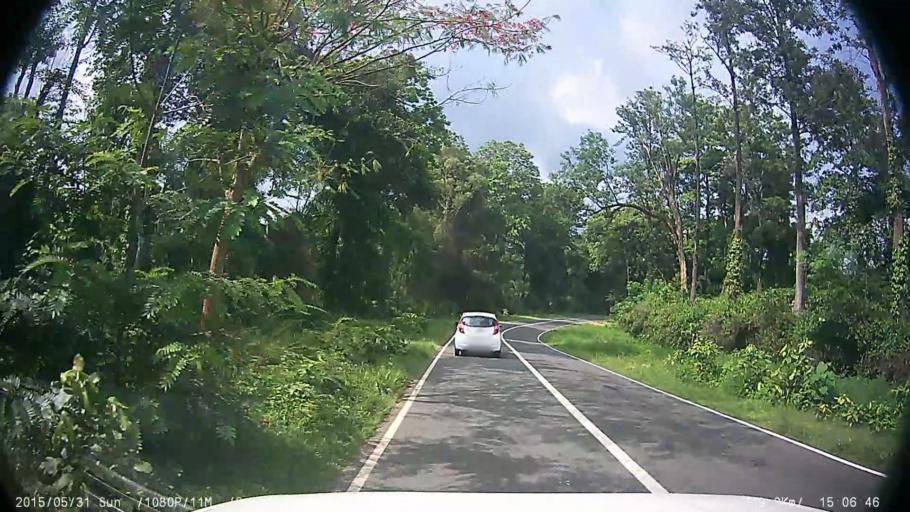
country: IN
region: Kerala
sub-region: Wayanad
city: Kalpetta
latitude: 11.6439
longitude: 76.2141
